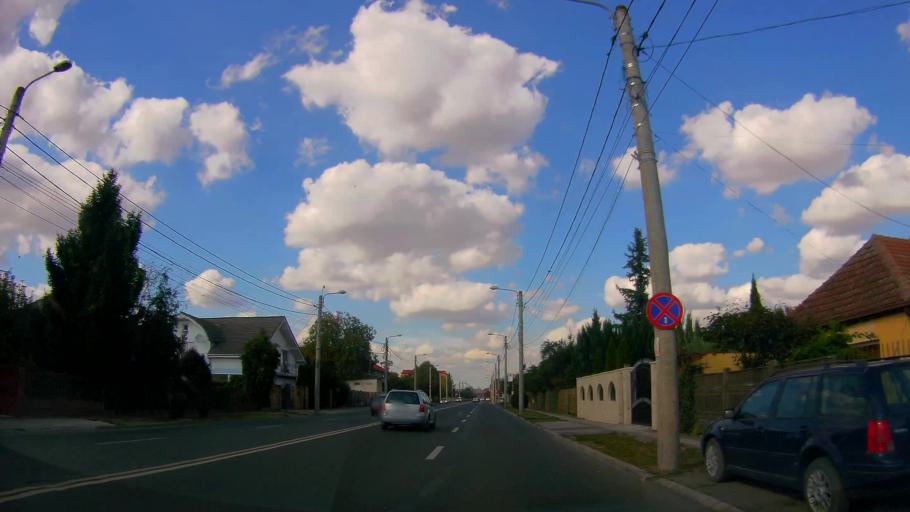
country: RO
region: Satu Mare
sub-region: Municipiul Satu Mare
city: Satu Mare
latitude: 47.7665
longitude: 22.8836
